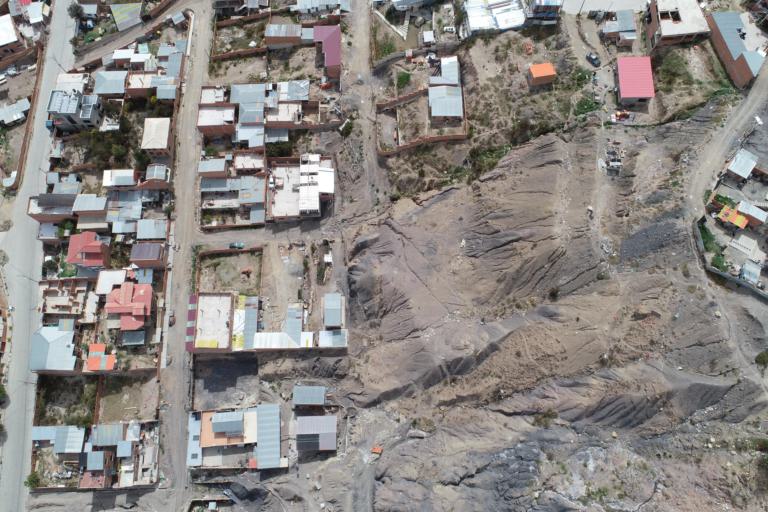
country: BO
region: La Paz
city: La Paz
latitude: -16.5521
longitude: -68.0532
